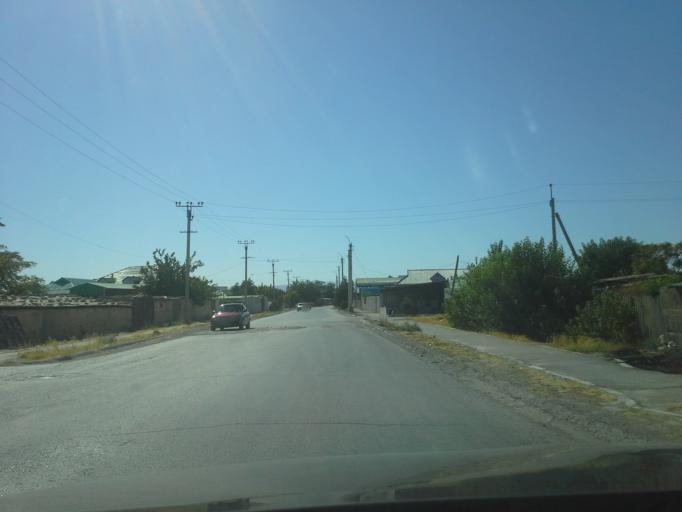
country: TM
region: Ahal
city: Abadan
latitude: 38.0766
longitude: 58.1643
